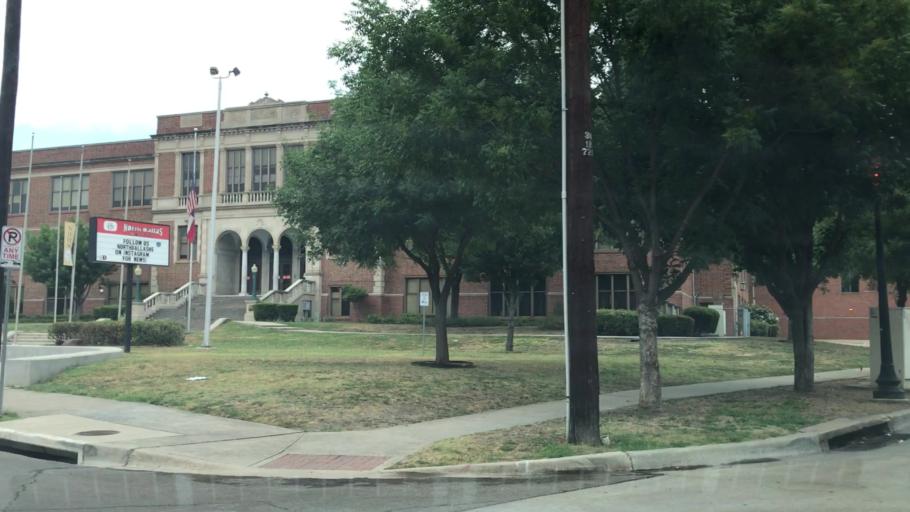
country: US
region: Texas
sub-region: Dallas County
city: Highland Park
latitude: 32.8095
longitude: -96.7949
